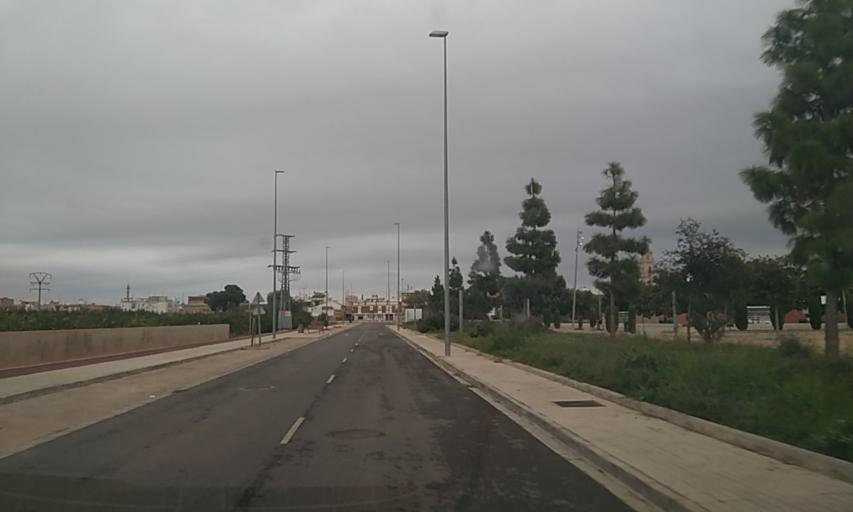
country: ES
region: Valencia
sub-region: Provincia de Valencia
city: L'Alcudia
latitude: 39.1953
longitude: -0.5123
